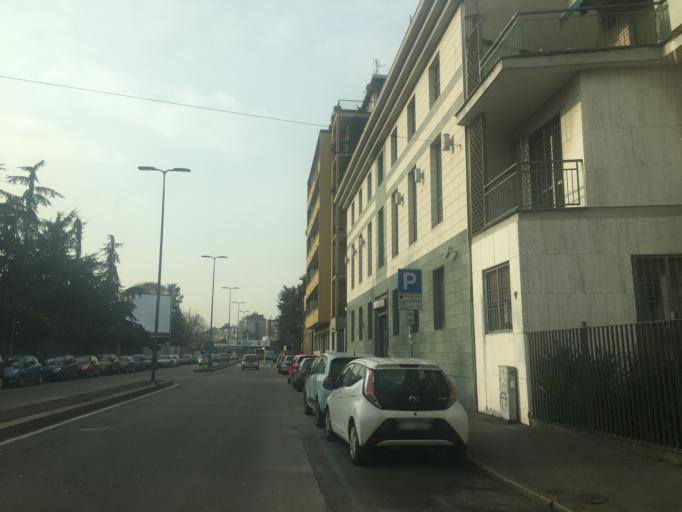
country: IT
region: Lombardy
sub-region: Citta metropolitana di Milano
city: Bresso
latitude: 45.5057
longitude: 9.2027
